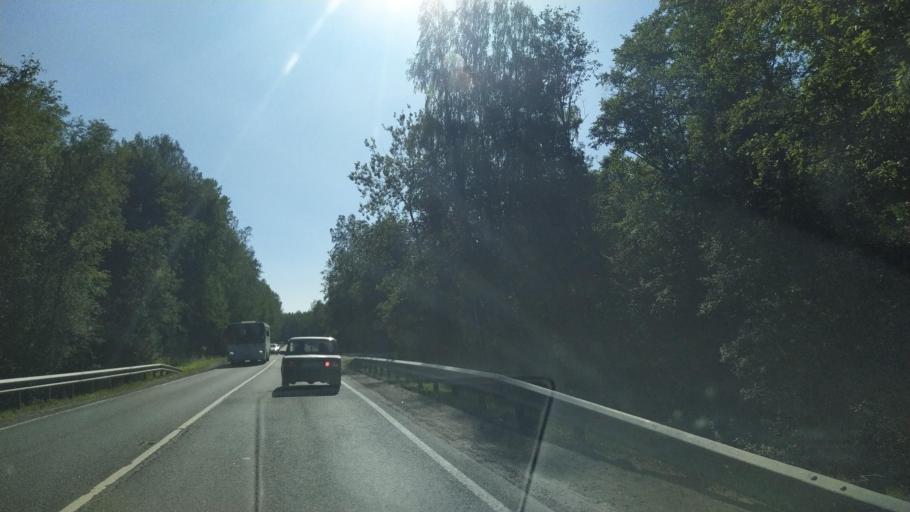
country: RU
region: Leningrad
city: Kirovsk
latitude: 59.9264
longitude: 30.9570
